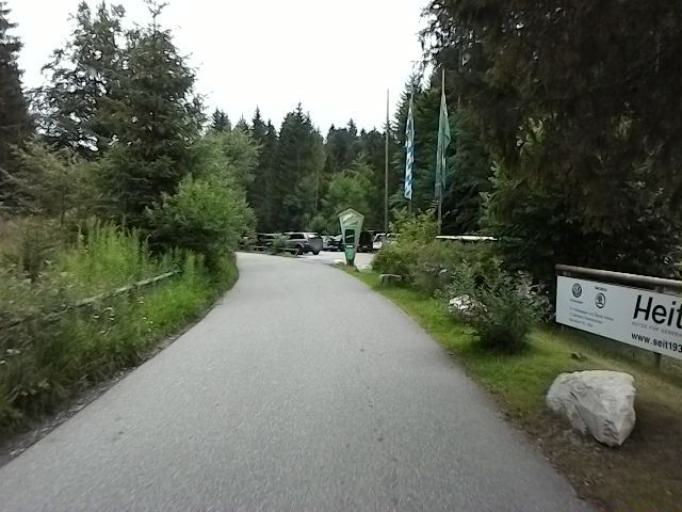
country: DE
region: Bavaria
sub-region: Upper Bavaria
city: Wallgau
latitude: 47.5268
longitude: 11.2947
